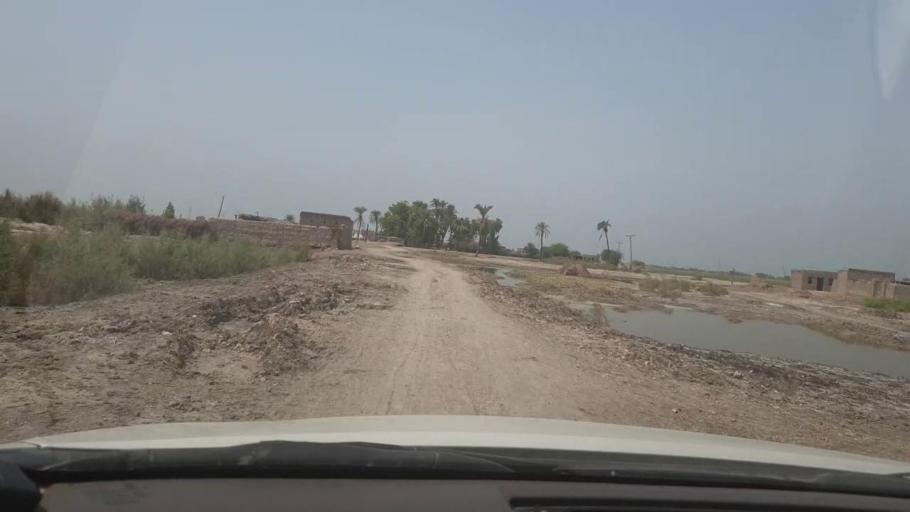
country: PK
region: Sindh
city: Shikarpur
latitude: 27.9612
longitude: 68.5912
